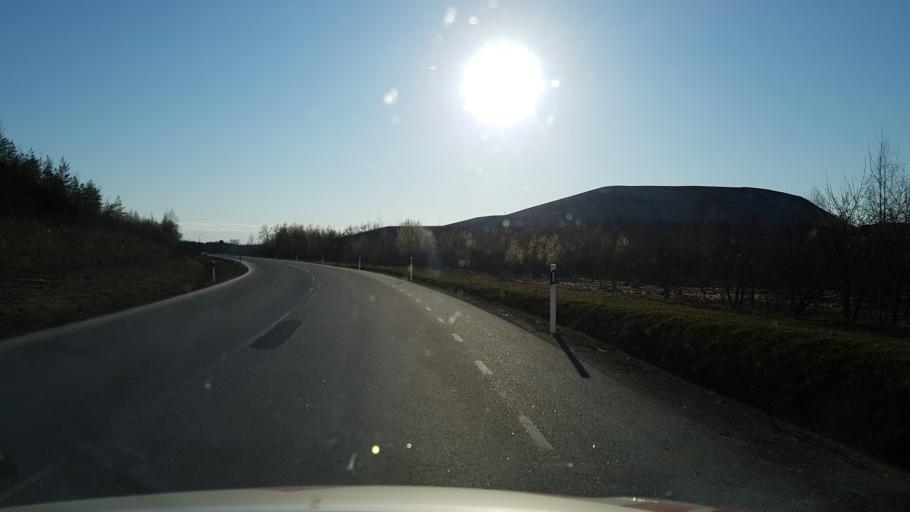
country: EE
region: Ida-Virumaa
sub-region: Kivioli linn
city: Kivioli
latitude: 59.3588
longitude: 26.9424
